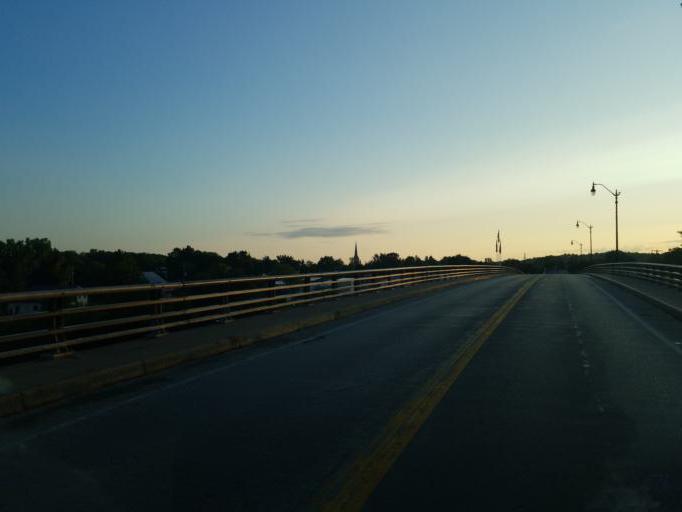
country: US
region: New York
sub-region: Wayne County
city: Clyde
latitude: 43.0807
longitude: -76.8720
